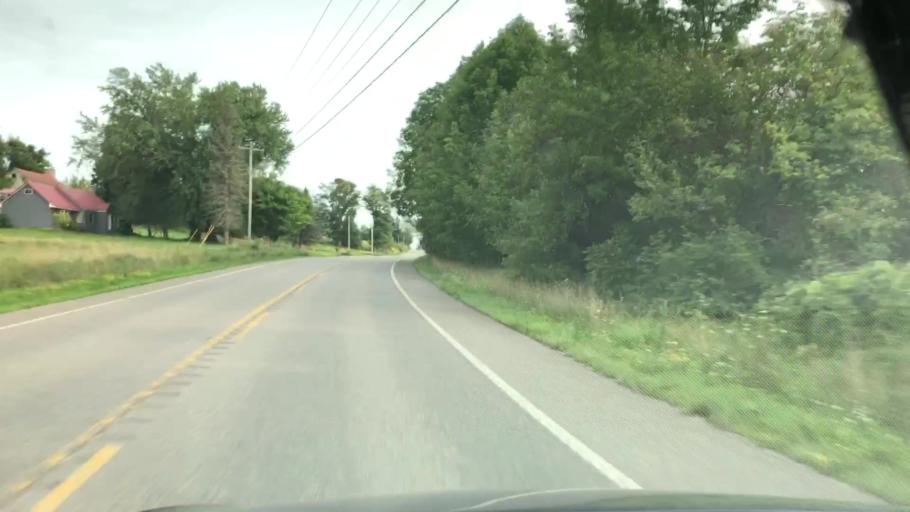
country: US
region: Pennsylvania
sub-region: Erie County
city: Union City
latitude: 41.8508
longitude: -79.8244
